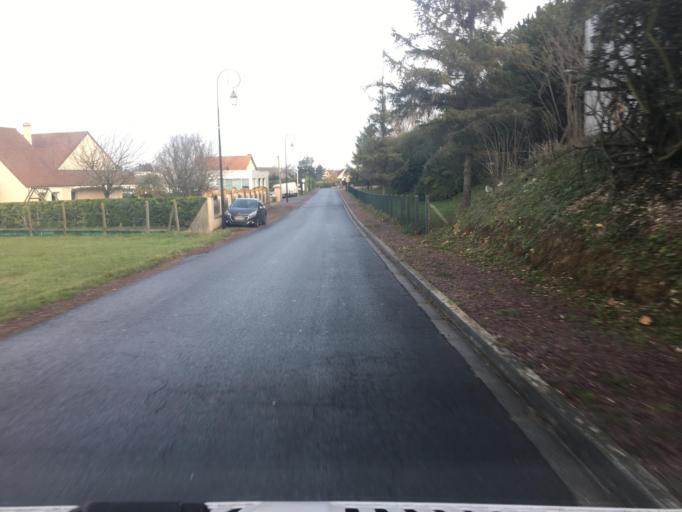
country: FR
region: Lower Normandy
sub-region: Departement du Calvados
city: Rots
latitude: 49.1996
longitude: -0.4627
